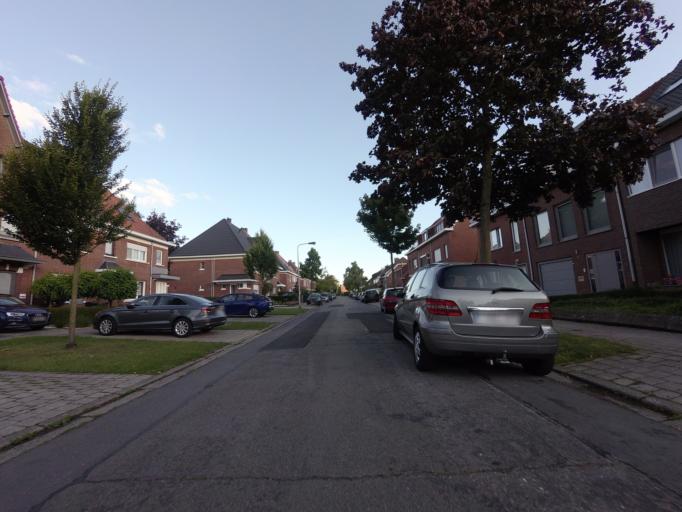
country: BE
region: Flanders
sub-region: Provincie Antwerpen
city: Edegem
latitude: 51.1597
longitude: 4.4310
